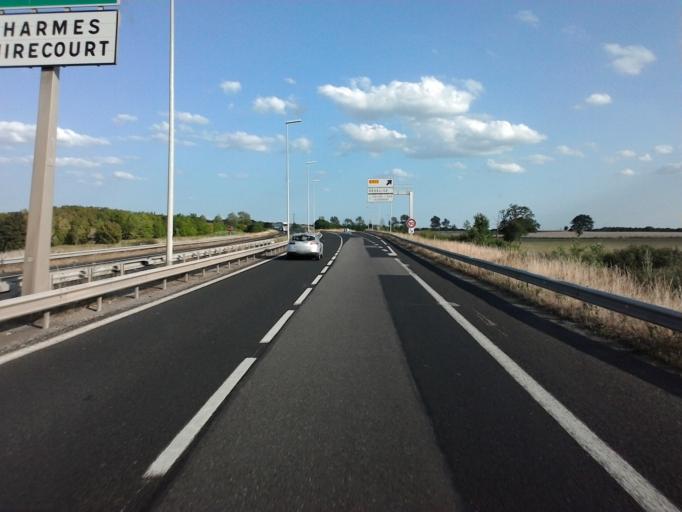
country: FR
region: Lorraine
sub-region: Departement de Meurthe-et-Moselle
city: Flavigny-sur-Moselle
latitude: 48.5544
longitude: 6.1883
